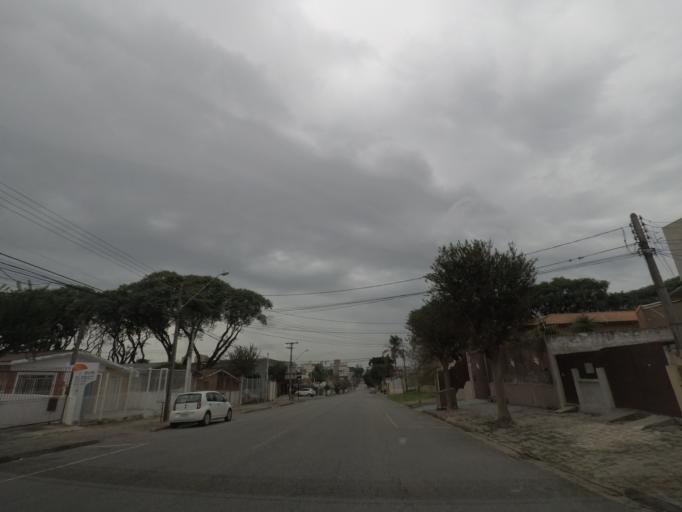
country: BR
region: Parana
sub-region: Curitiba
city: Curitiba
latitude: -25.4615
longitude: -49.2616
